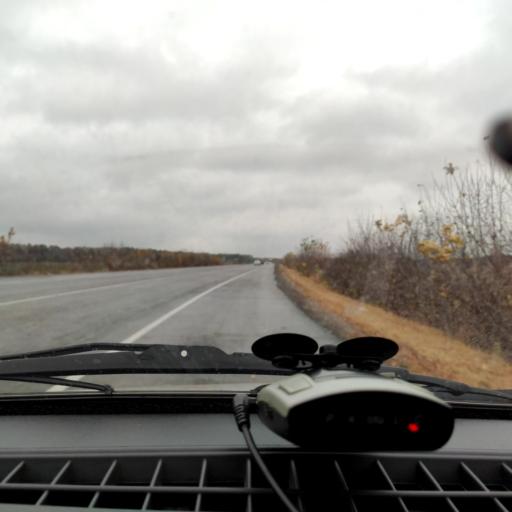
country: RU
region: Voronezj
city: Devitsa
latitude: 51.6041
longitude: 38.9716
